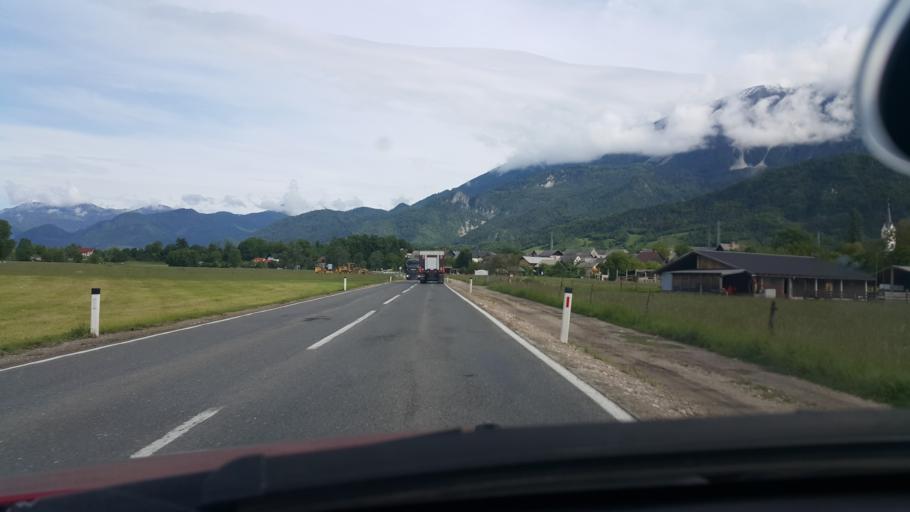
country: SI
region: Zirovnica
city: Zirovnica
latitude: 46.3843
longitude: 14.1477
